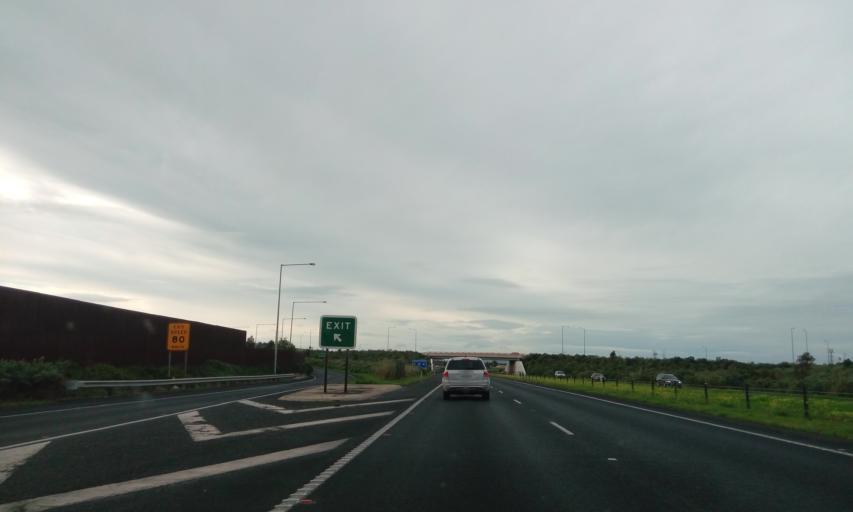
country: AU
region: Victoria
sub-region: Greater Geelong
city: Bell Post Hill
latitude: -38.0804
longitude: 144.3328
